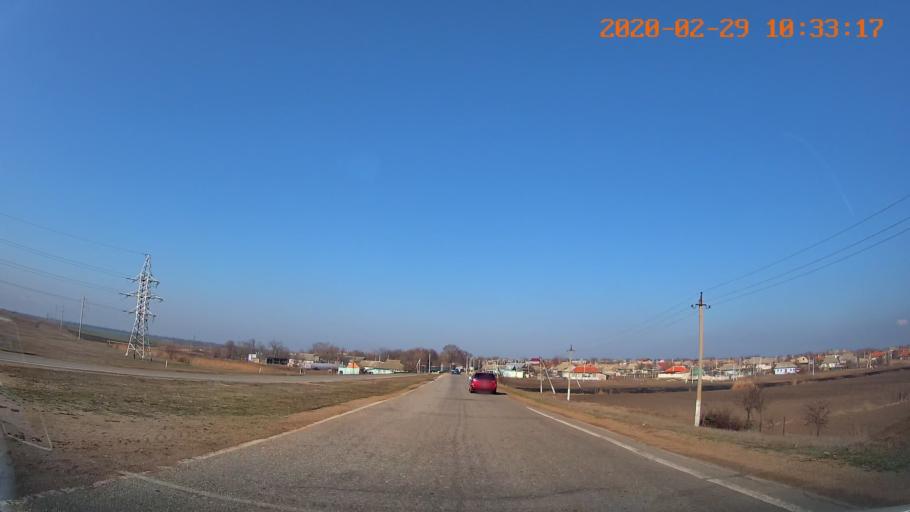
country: MD
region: Anenii Noi
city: Varnita
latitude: 46.9698
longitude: 29.5463
